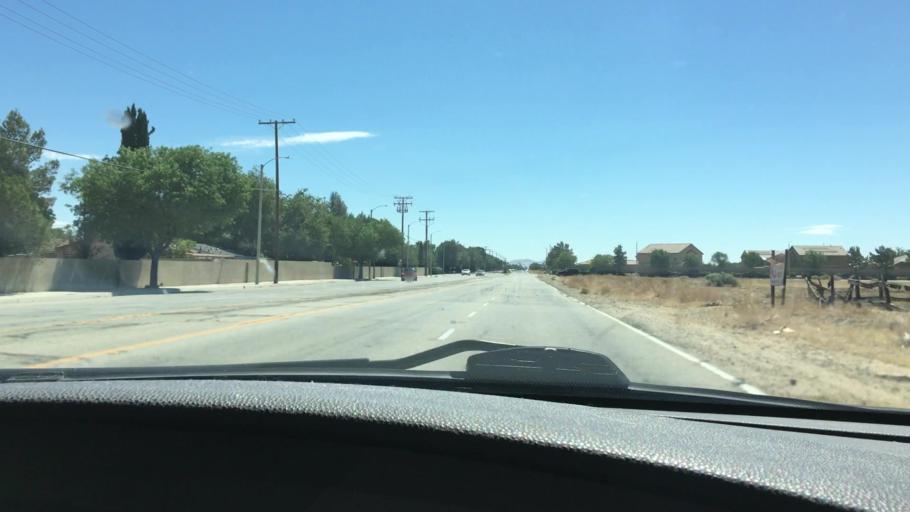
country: US
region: California
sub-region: Los Angeles County
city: Lancaster
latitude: 34.6751
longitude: -118.0880
